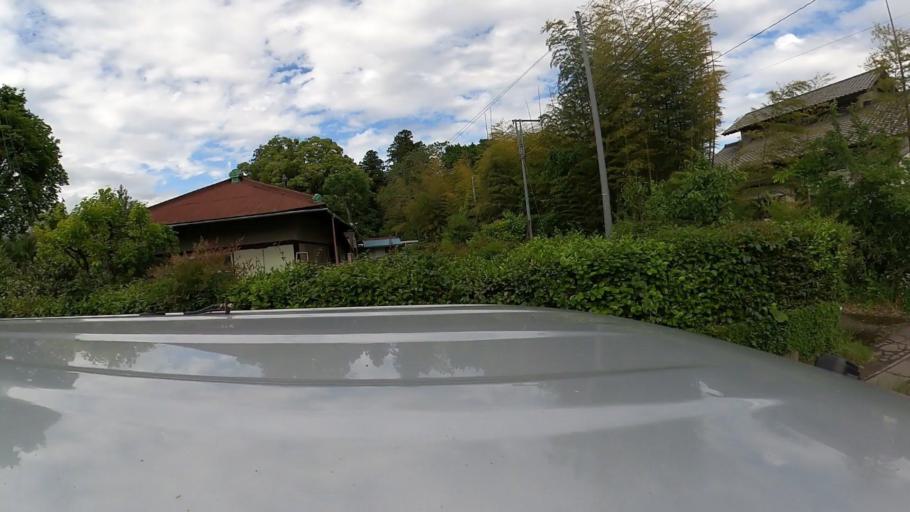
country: JP
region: Ibaraki
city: Ushiku
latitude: 35.9801
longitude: 140.1719
